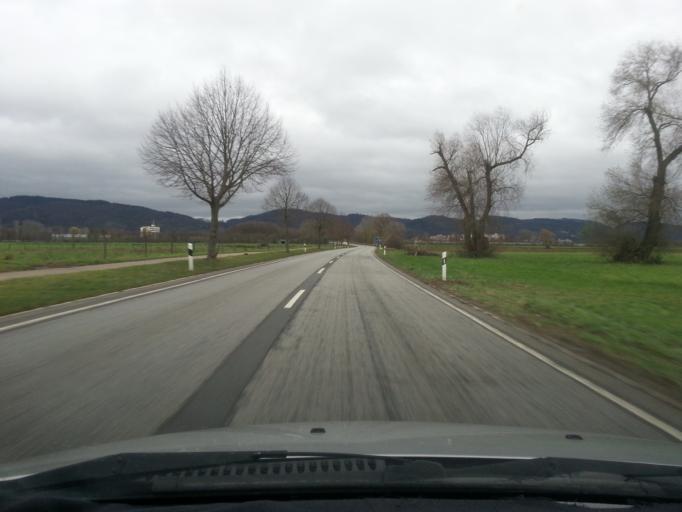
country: DE
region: Baden-Wuerttemberg
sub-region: Karlsruhe Region
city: Hemsbach
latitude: 49.5945
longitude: 8.6216
